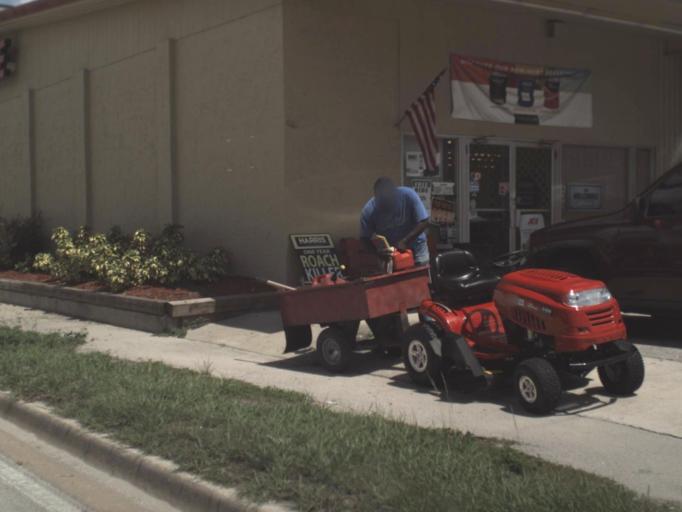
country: US
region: Florida
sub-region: Polk County
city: Fort Meade
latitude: 27.7561
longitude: -81.8014
